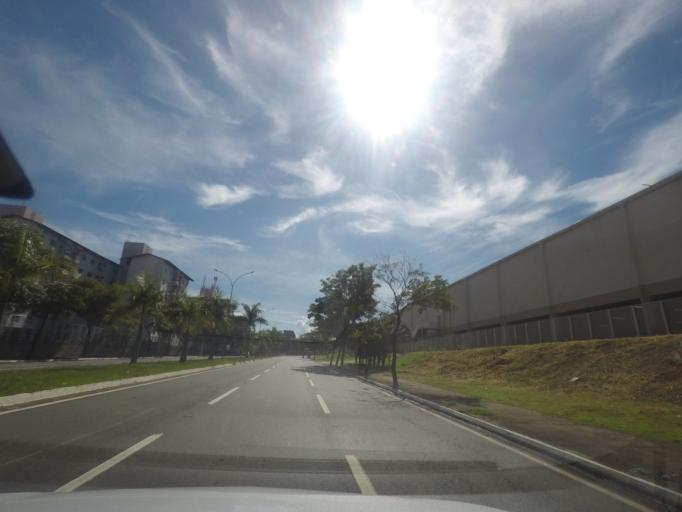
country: BR
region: Goias
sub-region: Goiania
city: Goiania
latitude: -16.6644
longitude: -49.2654
